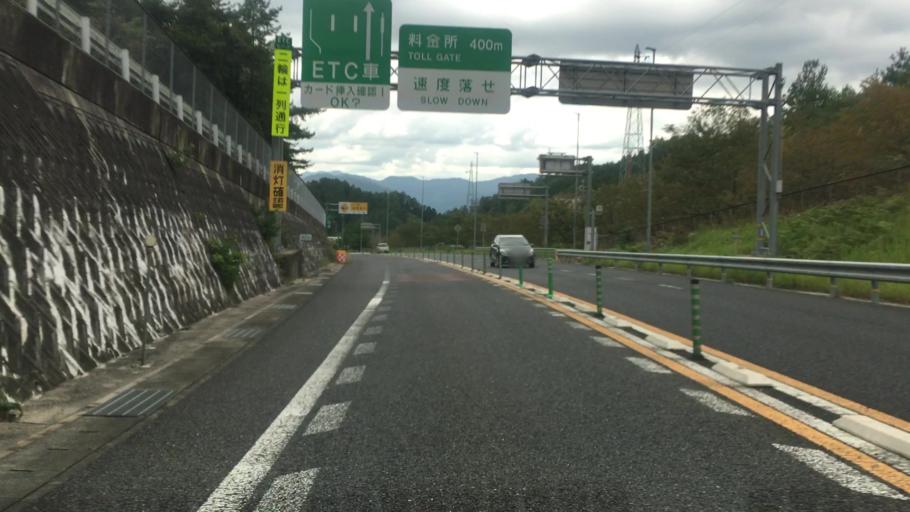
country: JP
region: Kyoto
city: Fukuchiyama
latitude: 35.3034
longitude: 134.9273
